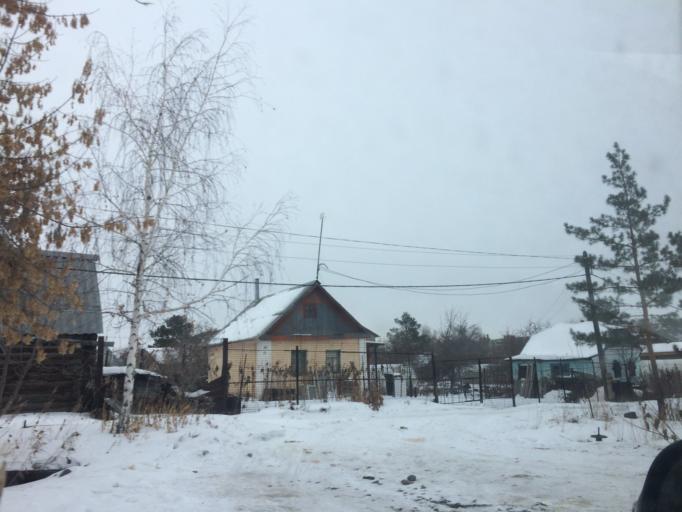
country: RU
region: Chelyabinsk
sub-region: Gorod Magnitogorsk
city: Magnitogorsk
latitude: 53.3578
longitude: 58.9882
